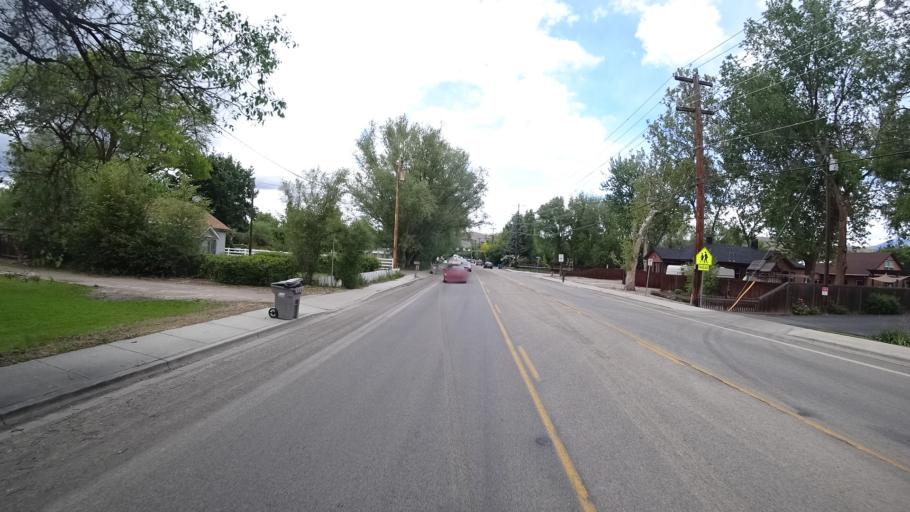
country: US
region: Idaho
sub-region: Ada County
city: Garden City
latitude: 43.6417
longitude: -116.2335
